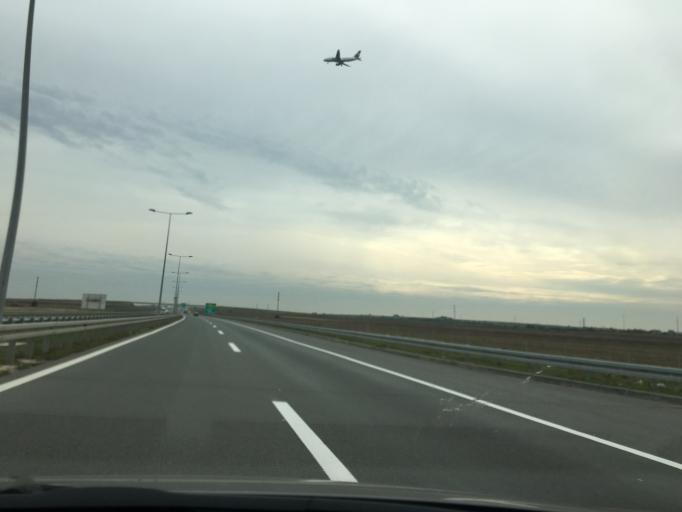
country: RS
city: Dobanovci
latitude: 44.8504
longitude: 20.2491
